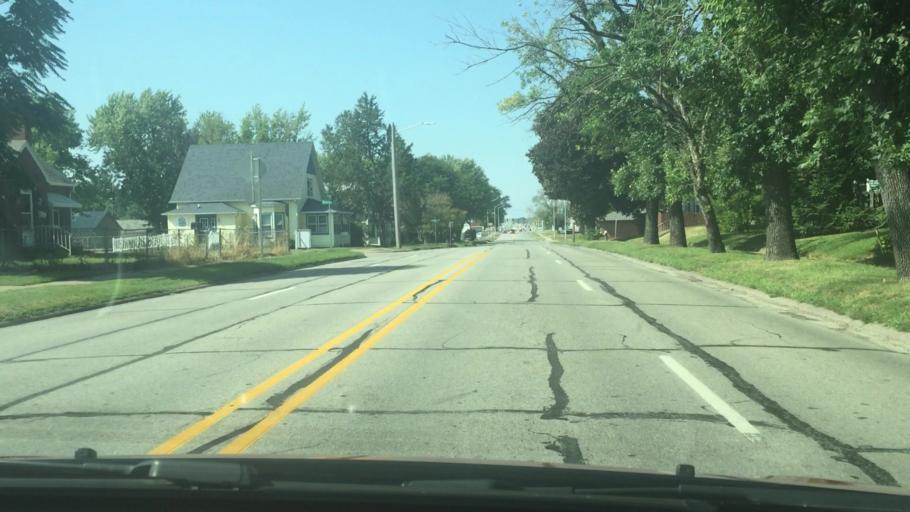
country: US
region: Iowa
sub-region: Muscatine County
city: Muscatine
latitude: 41.4378
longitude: -91.0307
